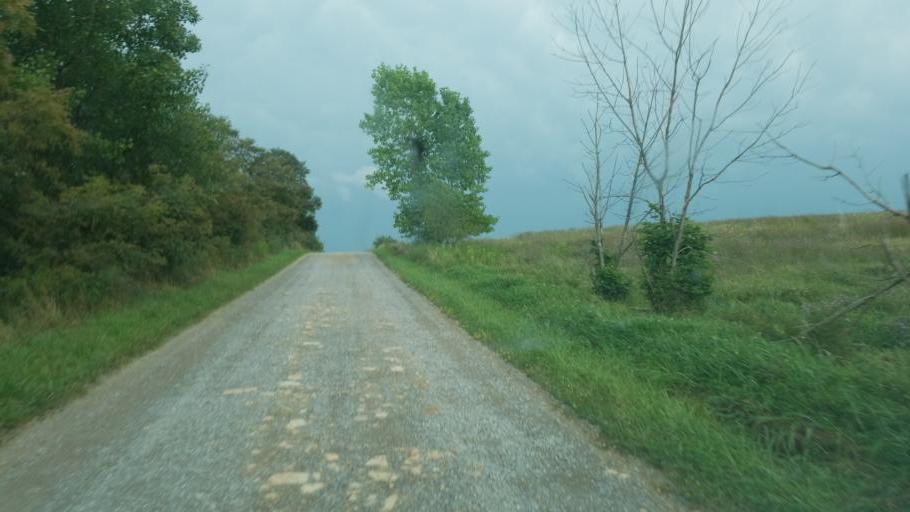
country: US
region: Pennsylvania
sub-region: Clarion County
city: Knox
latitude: 41.1455
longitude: -79.5081
